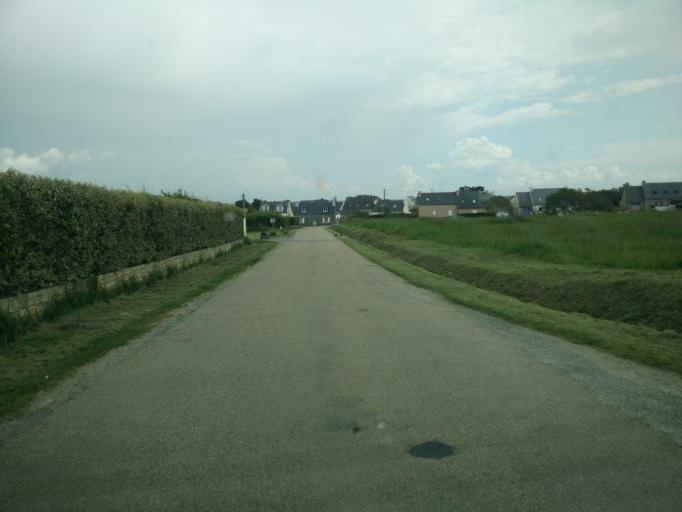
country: FR
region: Brittany
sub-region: Departement du Finistere
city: Camaret-sur-Mer
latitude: 48.2743
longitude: -4.6093
